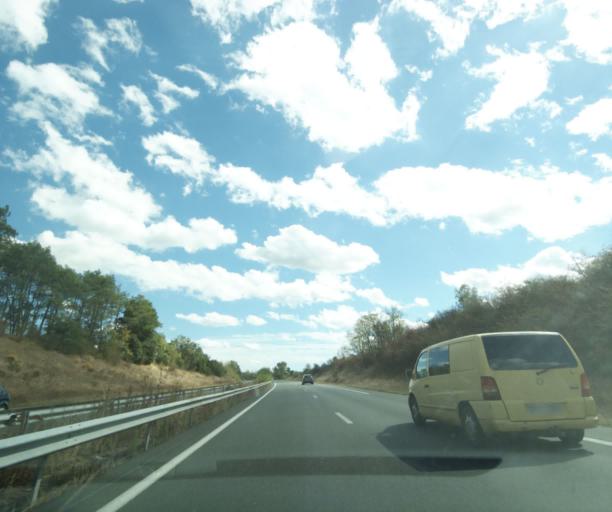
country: FR
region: Aquitaine
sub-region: Departement du Lot-et-Garonne
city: Fourques-sur-Garonne
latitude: 44.4535
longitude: 0.0876
